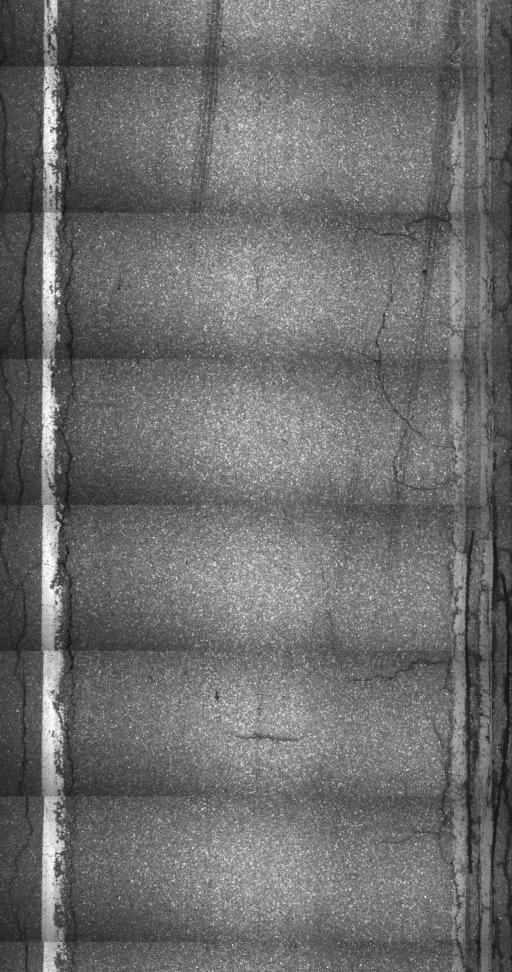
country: US
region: Vermont
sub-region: Addison County
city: Bristol
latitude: 44.1621
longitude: -73.0511
